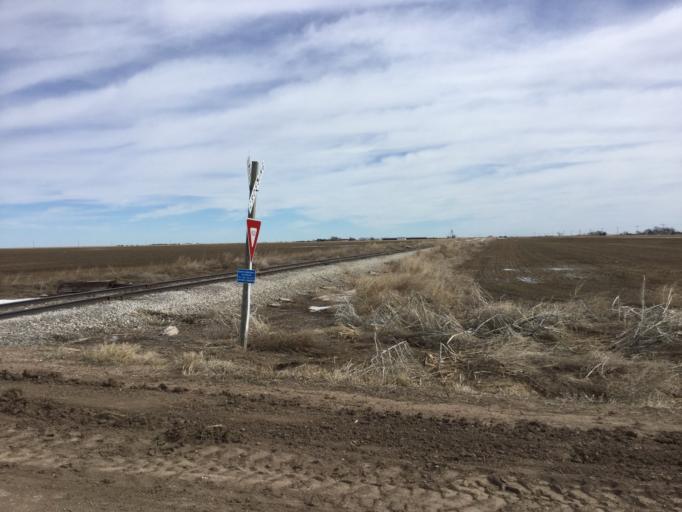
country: US
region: Kansas
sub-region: Lane County
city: Dighton
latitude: 38.4826
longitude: -100.5758
